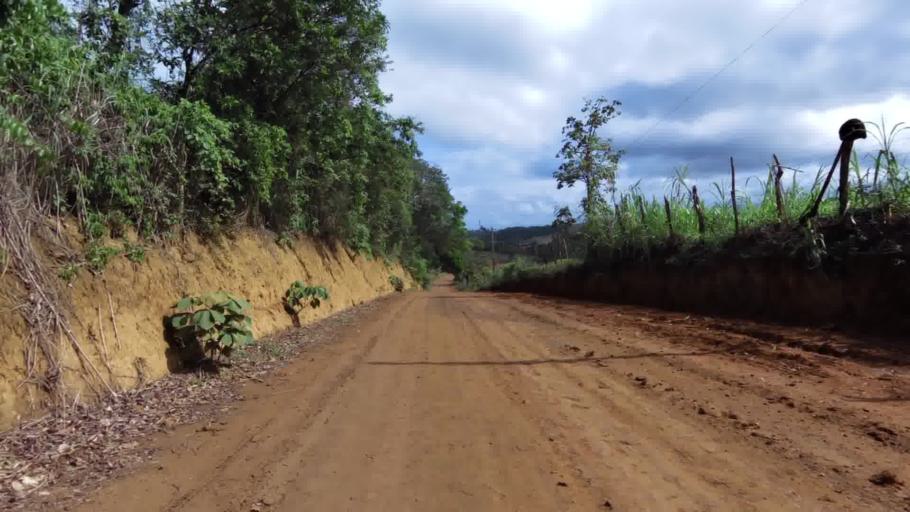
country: BR
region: Espirito Santo
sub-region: Piuma
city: Piuma
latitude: -20.8110
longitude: -40.6667
